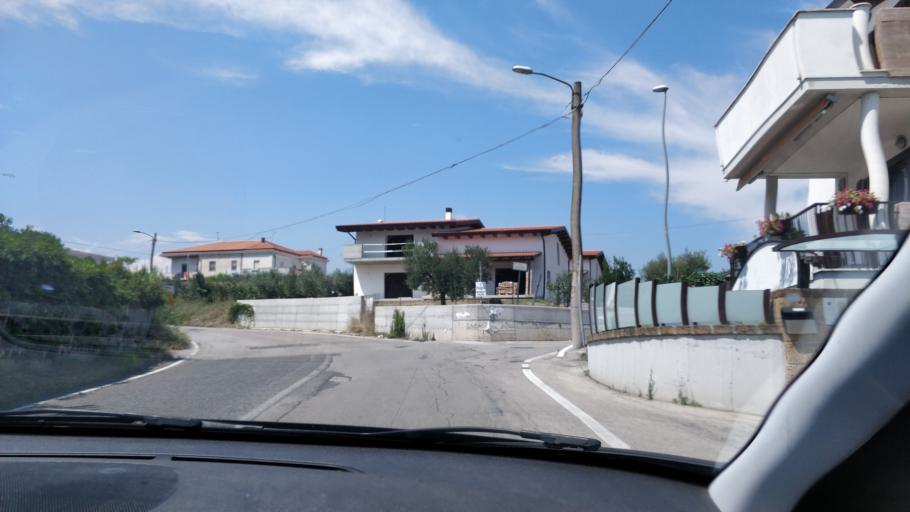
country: IT
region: Abruzzo
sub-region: Provincia di Chieti
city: Francavilla al Mare
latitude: 42.4243
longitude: 14.2694
